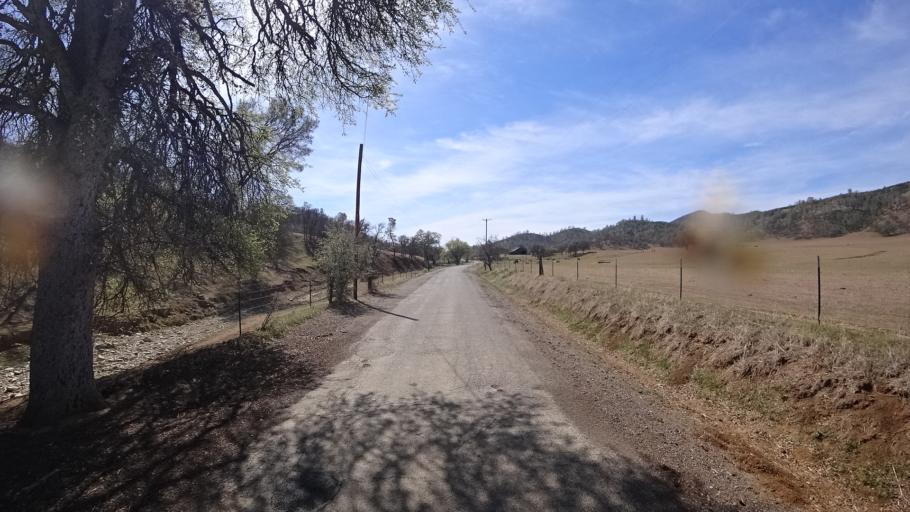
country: US
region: California
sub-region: Glenn County
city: Willows
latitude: 39.4712
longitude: -122.4487
